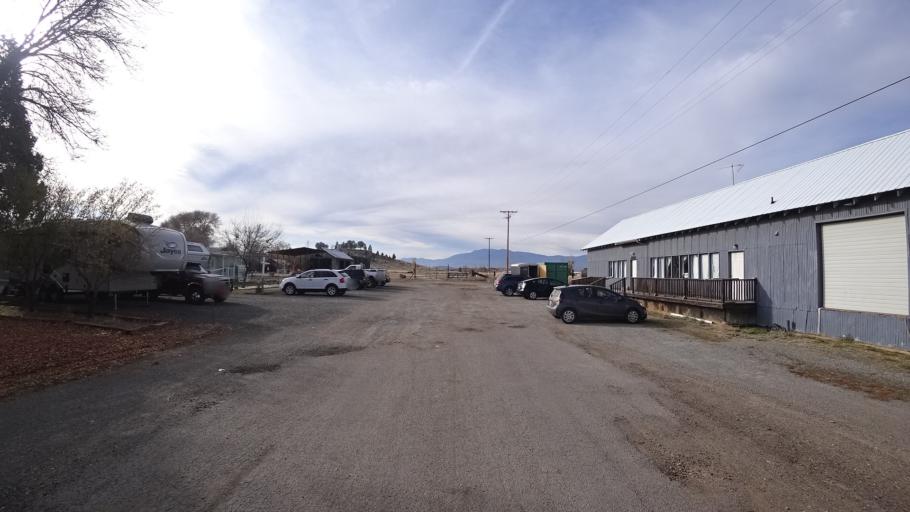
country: US
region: California
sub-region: Siskiyou County
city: Montague
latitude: 41.7245
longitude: -122.5282
